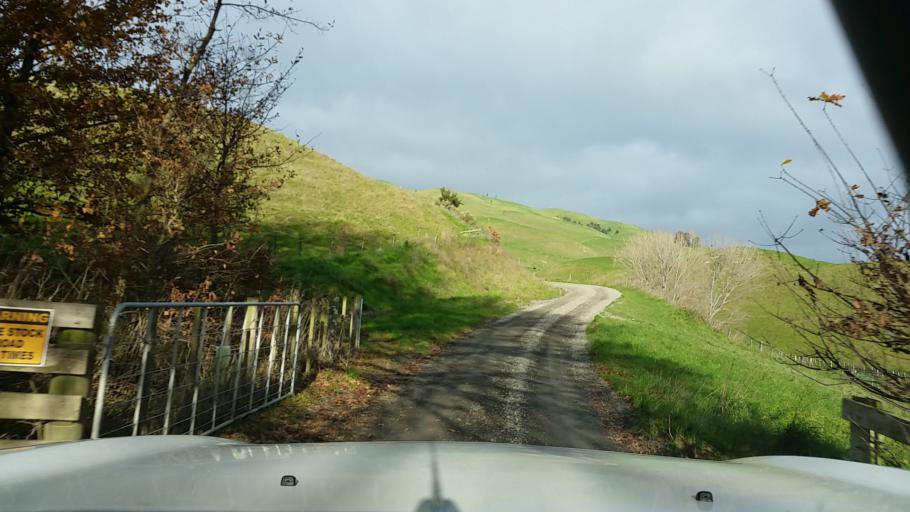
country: NZ
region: Wellington
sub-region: Masterton District
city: Masterton
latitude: -41.0342
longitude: 175.7040
